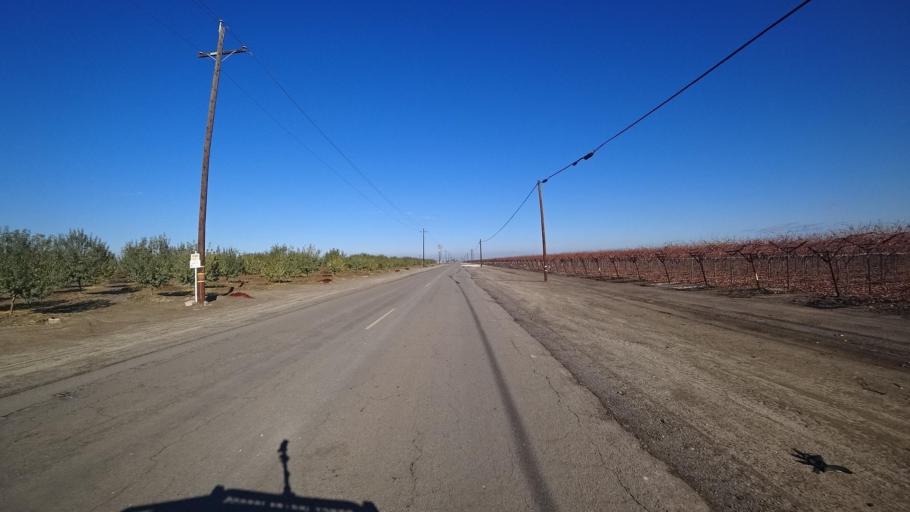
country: US
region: California
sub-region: Kern County
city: McFarland
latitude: 35.7121
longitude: -119.2764
